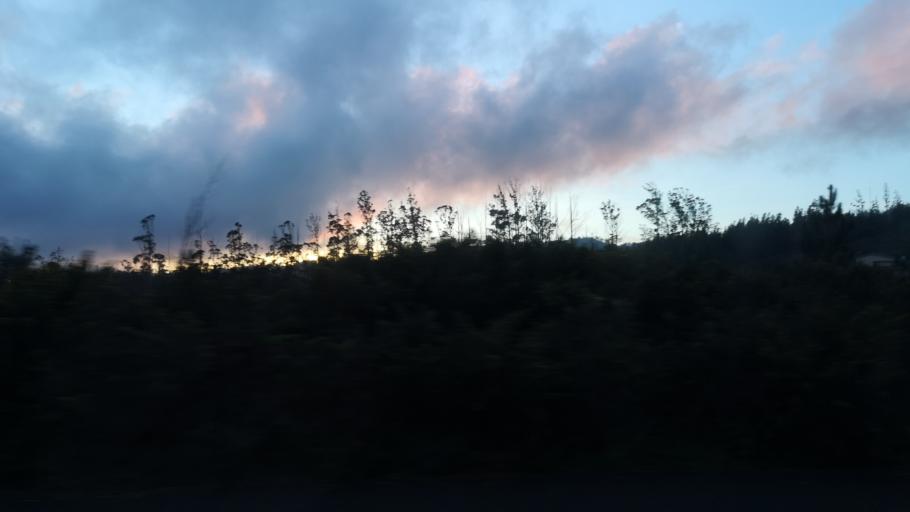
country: PT
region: Madeira
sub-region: Santa Cruz
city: Camacha
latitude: 32.6934
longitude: -16.8348
